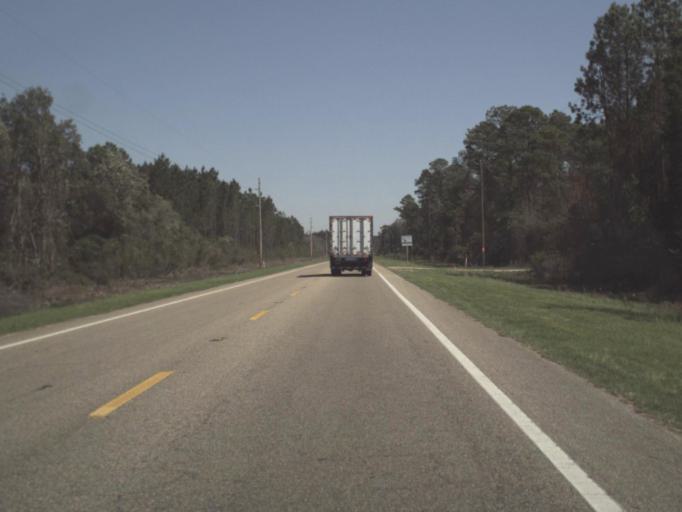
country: US
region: Florida
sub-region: Liberty County
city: Bristol
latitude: 30.4175
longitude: -84.8785
